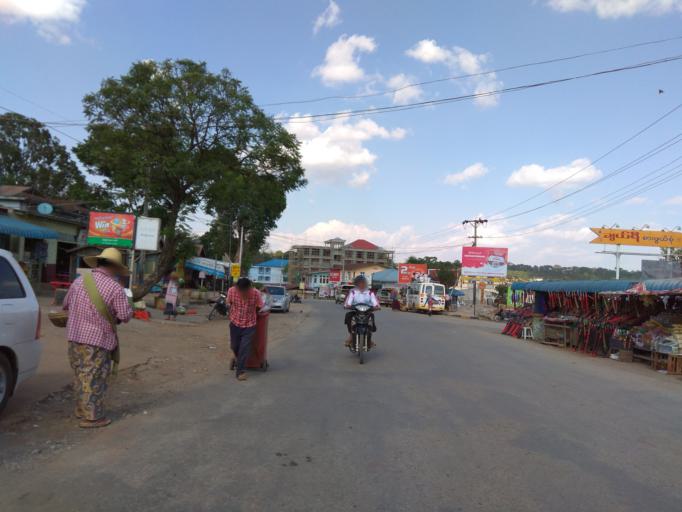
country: MM
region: Shan
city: Taunggyi
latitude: 20.6559
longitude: 96.6405
